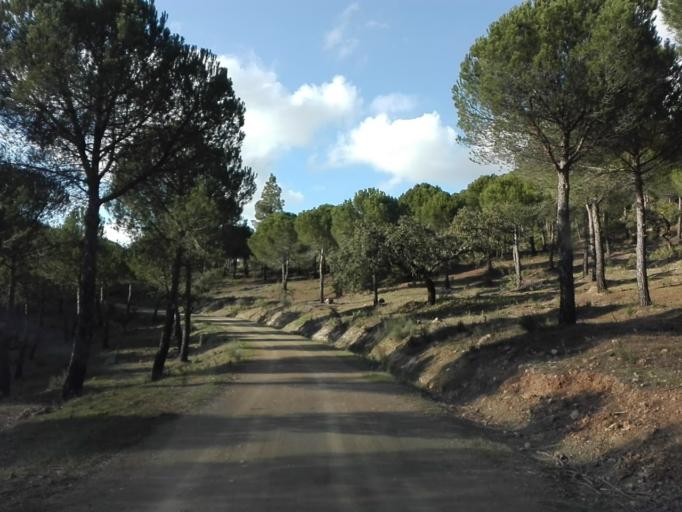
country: ES
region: Extremadura
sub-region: Provincia de Badajoz
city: Casas de Reina
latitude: 38.1782
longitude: -5.9741
